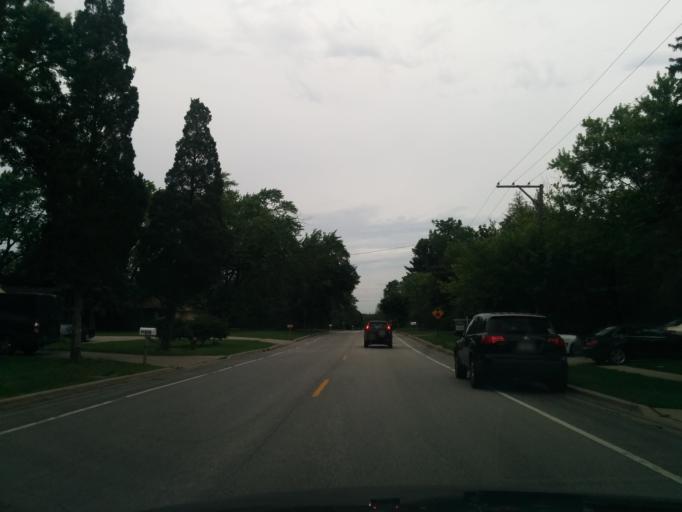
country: US
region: Illinois
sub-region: DuPage County
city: Oakbrook Terrace
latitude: 41.8627
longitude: -87.9731
